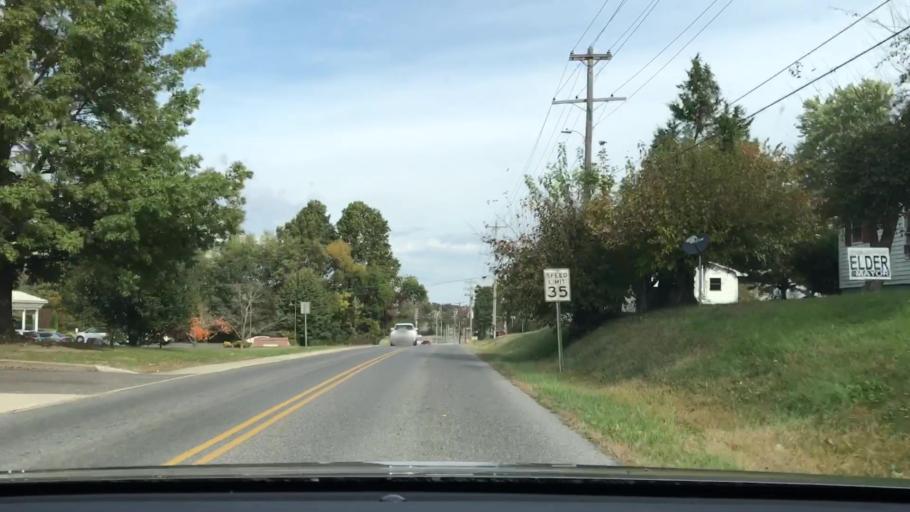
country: US
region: Kentucky
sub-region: Graves County
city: Mayfield
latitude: 36.7466
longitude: -88.6495
